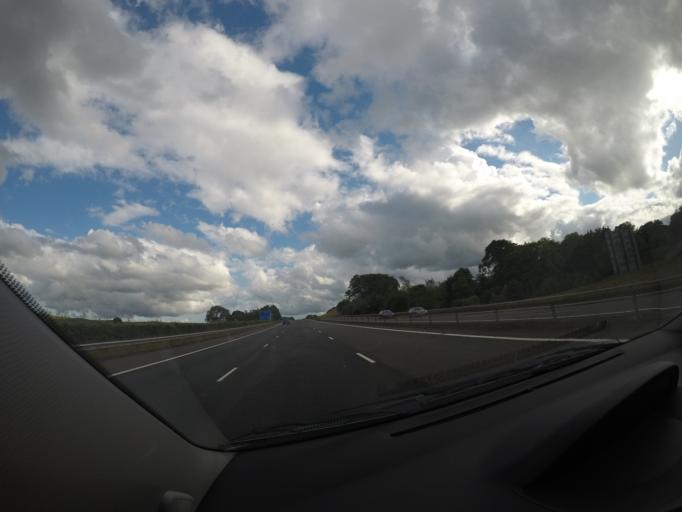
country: GB
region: Scotland
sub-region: Dumfries and Galloway
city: Lochmaben
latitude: 55.2274
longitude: -3.4130
